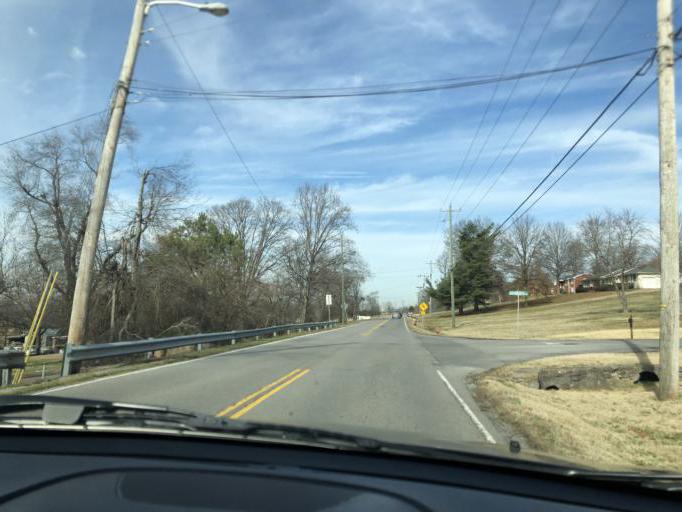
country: US
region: Tennessee
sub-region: Davidson County
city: Lakewood
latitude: 36.2109
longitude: -86.6868
